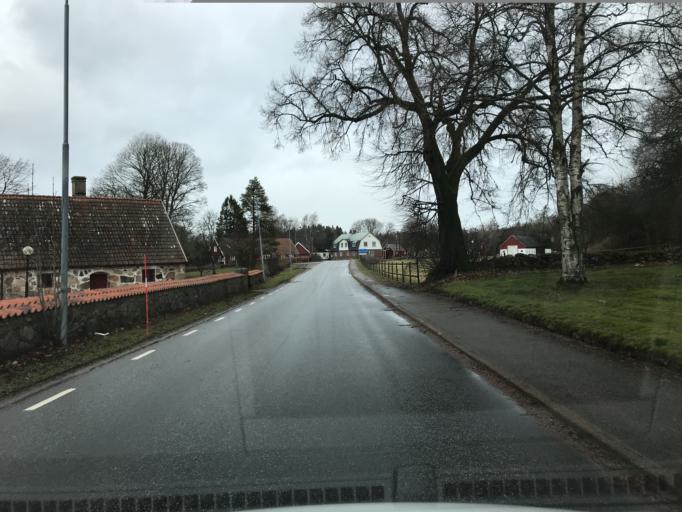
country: SE
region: Skane
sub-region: Hoors Kommun
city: Hoeoer
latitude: 56.0201
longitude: 13.5097
